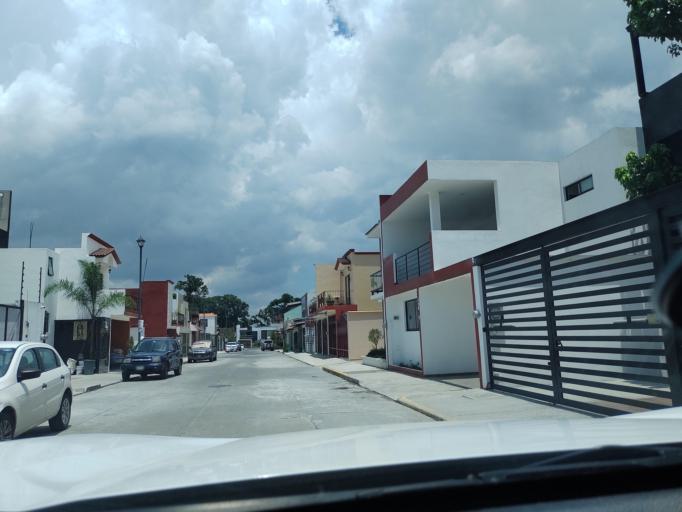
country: MX
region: Veracruz
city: Coatepec
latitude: 19.4478
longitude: -96.9503
